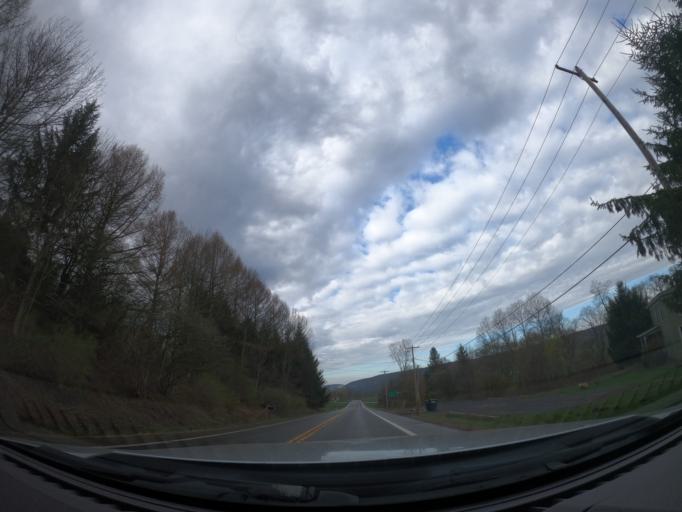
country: US
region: New York
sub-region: Madison County
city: Cazenovia
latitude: 42.7426
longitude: -75.9426
